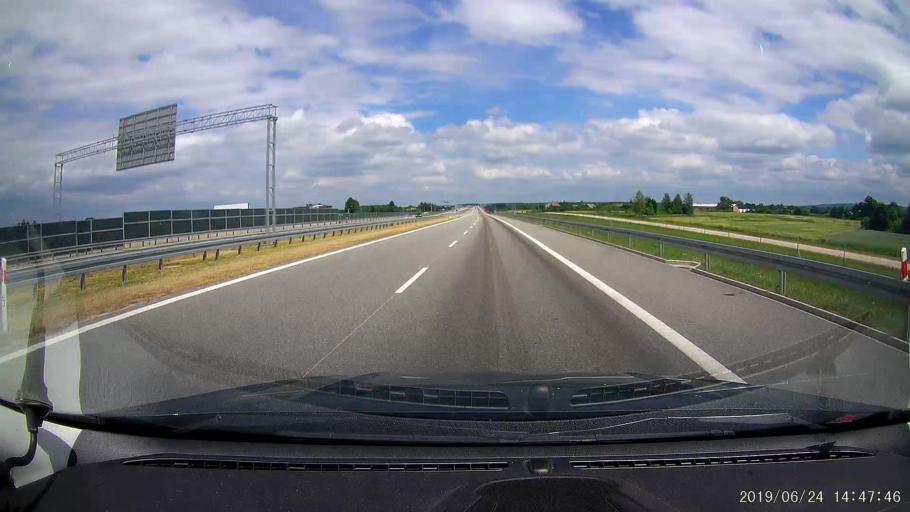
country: PL
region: Subcarpathian Voivodeship
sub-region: Powiat debicki
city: Zyrakow
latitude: 50.0813
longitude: 21.4087
